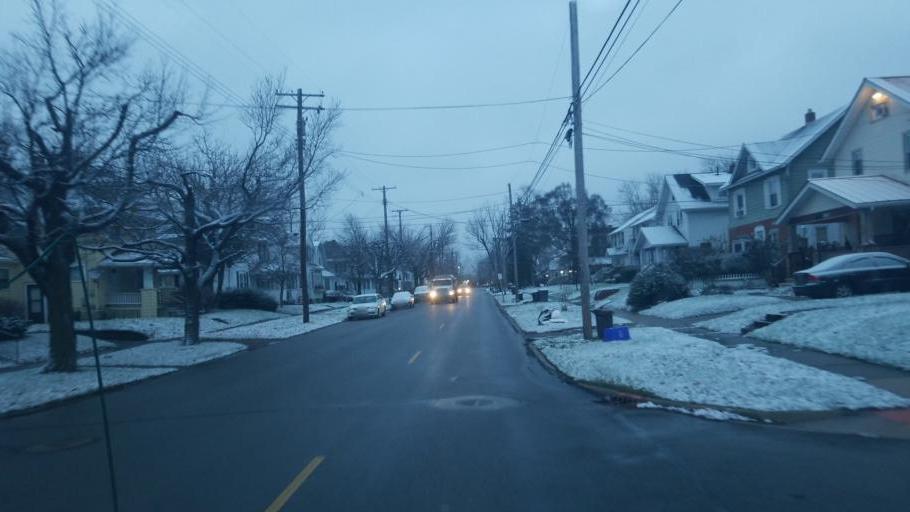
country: US
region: Ohio
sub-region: Marion County
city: Marion
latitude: 40.5879
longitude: -83.1012
